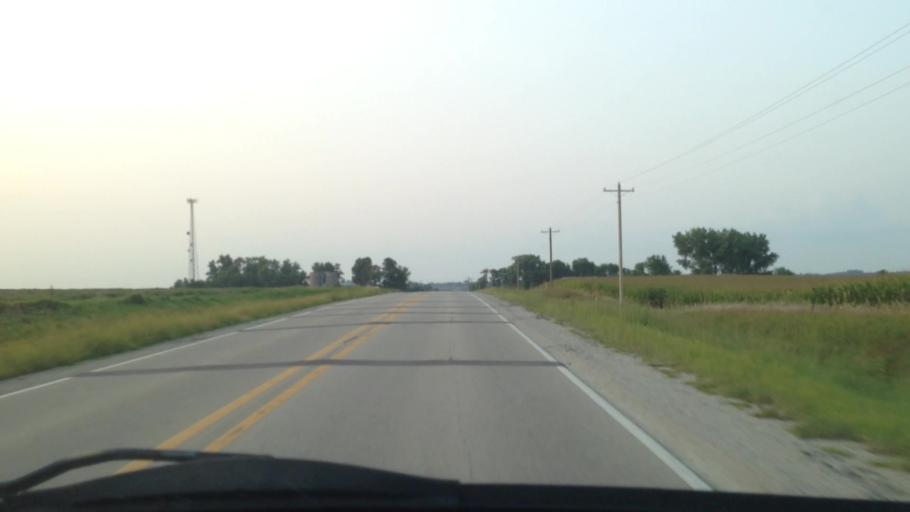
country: US
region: Iowa
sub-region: Linn County
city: Palo
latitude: 42.0750
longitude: -91.8691
